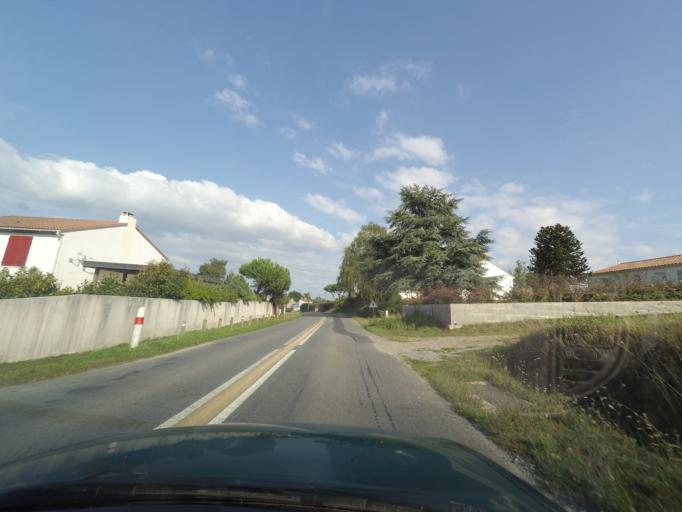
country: FR
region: Pays de la Loire
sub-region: Departement de la Loire-Atlantique
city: Saint-Philbert-de-Grand-Lieu
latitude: 47.0349
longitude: -1.6706
